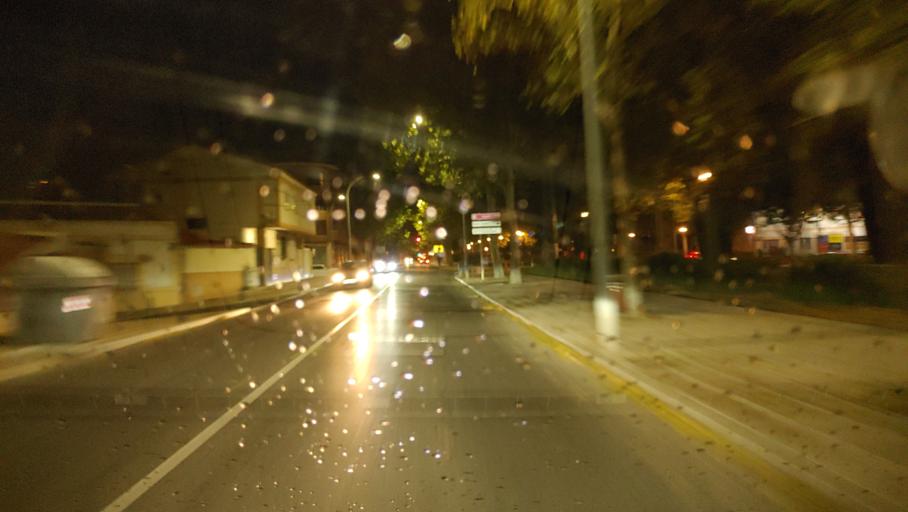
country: ES
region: Castille-La Mancha
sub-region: Provincia de Ciudad Real
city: Ciudad Real
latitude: 38.9757
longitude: -3.9274
